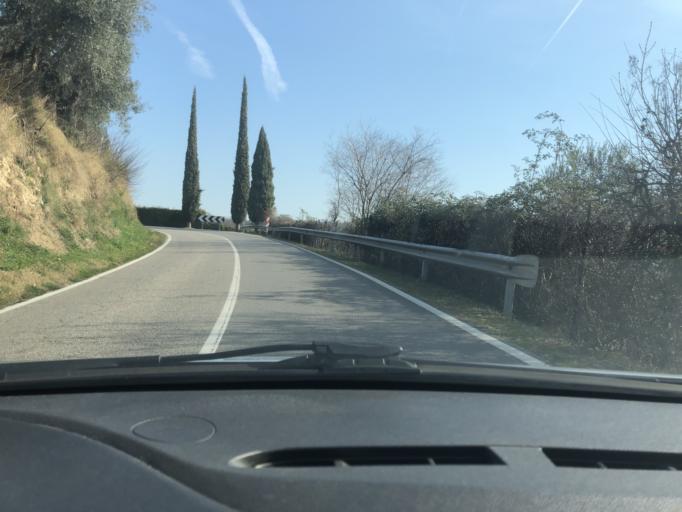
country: IT
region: Veneto
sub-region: Provincia di Verona
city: Garda
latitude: 45.5642
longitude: 10.7294
